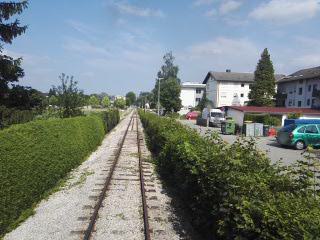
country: DE
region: Bavaria
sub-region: Upper Bavaria
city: Prien am Chiemsee
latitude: 47.8604
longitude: 12.3592
